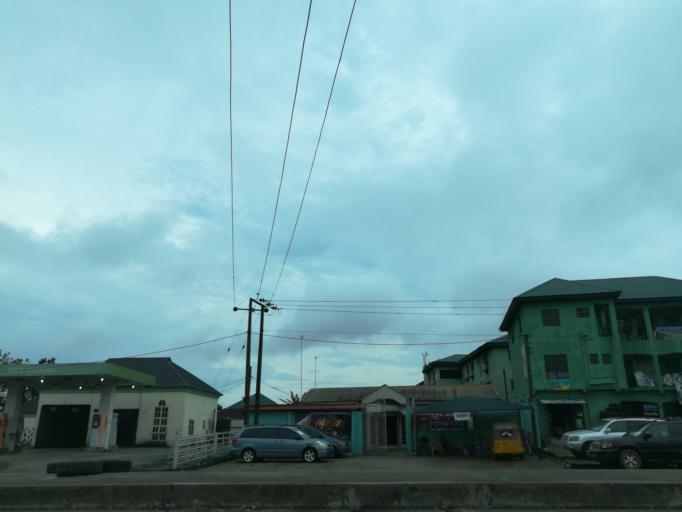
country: NG
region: Rivers
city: Port Harcourt
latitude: 4.8622
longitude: 7.0372
